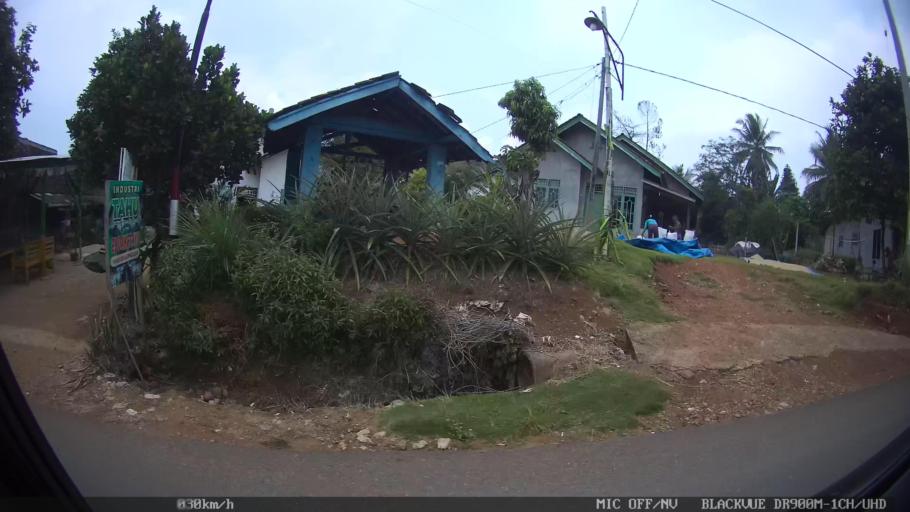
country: ID
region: Lampung
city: Gadingrejo
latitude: -5.3909
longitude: 105.0416
